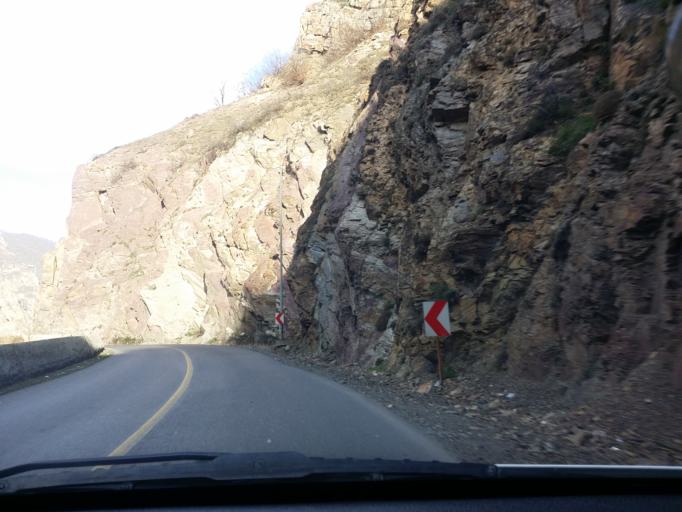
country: IR
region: Mazandaran
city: Chalus
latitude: 36.2640
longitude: 51.2639
